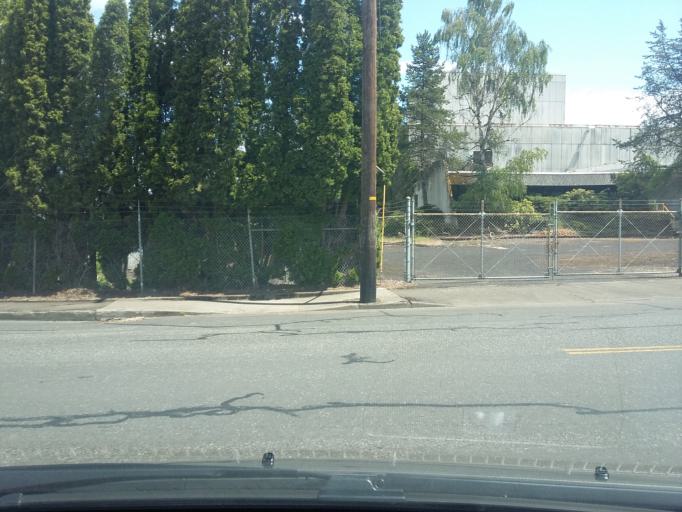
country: US
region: Washington
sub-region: Clark County
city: Camas
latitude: 45.5871
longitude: -122.4143
